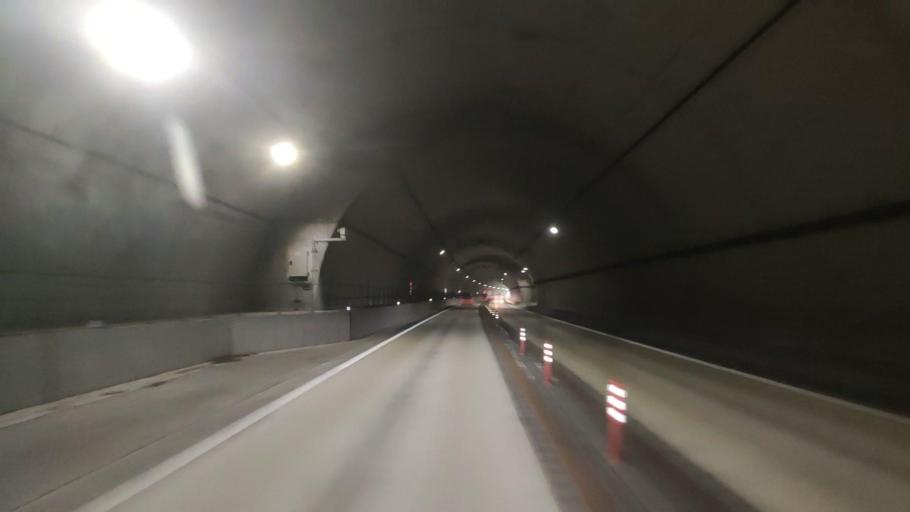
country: JP
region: Wakayama
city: Tanabe
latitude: 33.5933
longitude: 135.4371
